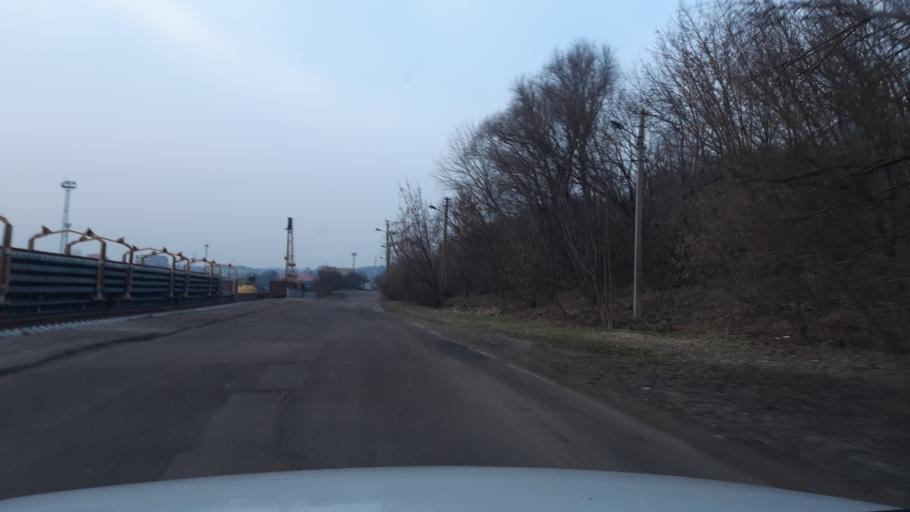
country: LT
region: Kauno apskritis
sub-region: Kaunas
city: Aleksotas
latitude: 54.8809
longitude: 23.9357
